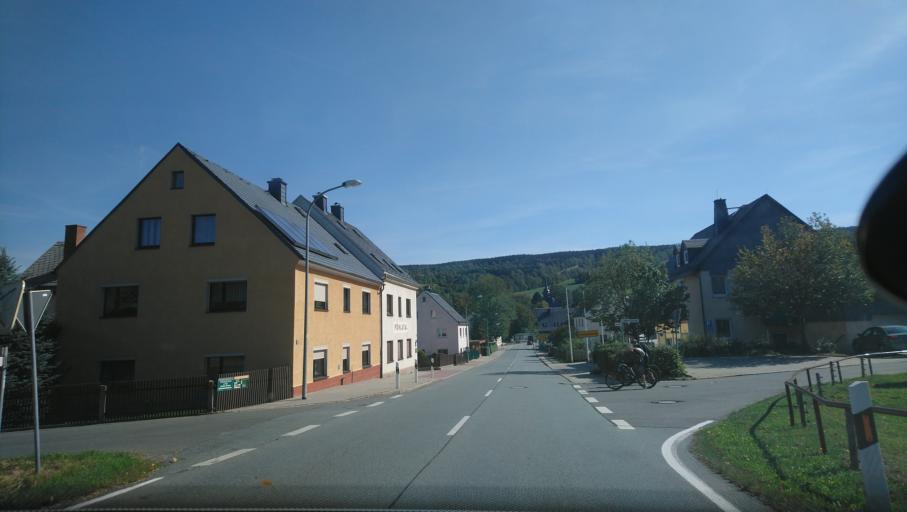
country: DE
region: Saxony
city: Konigswalde
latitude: 50.5467
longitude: 13.0440
